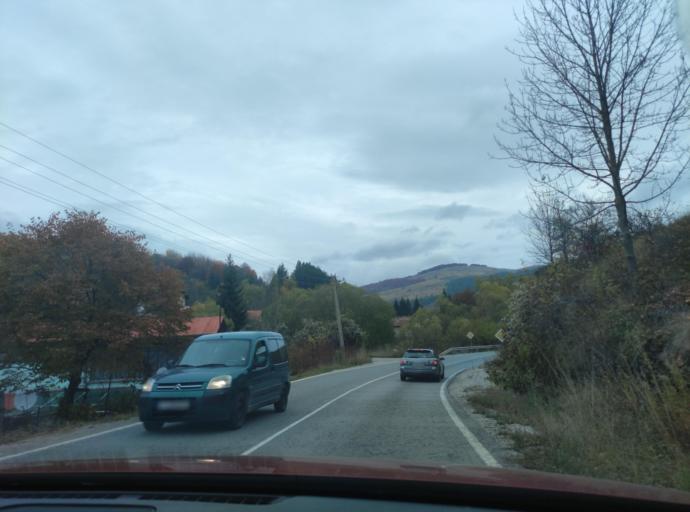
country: BG
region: Sofiya
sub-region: Obshtina Godech
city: Godech
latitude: 43.0694
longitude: 23.1078
